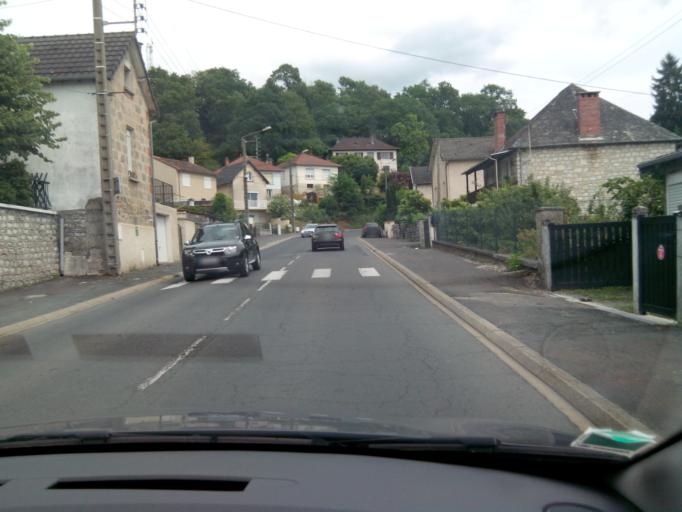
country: FR
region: Limousin
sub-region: Departement de la Correze
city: Brive-la-Gaillarde
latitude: 45.1485
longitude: 1.5454
